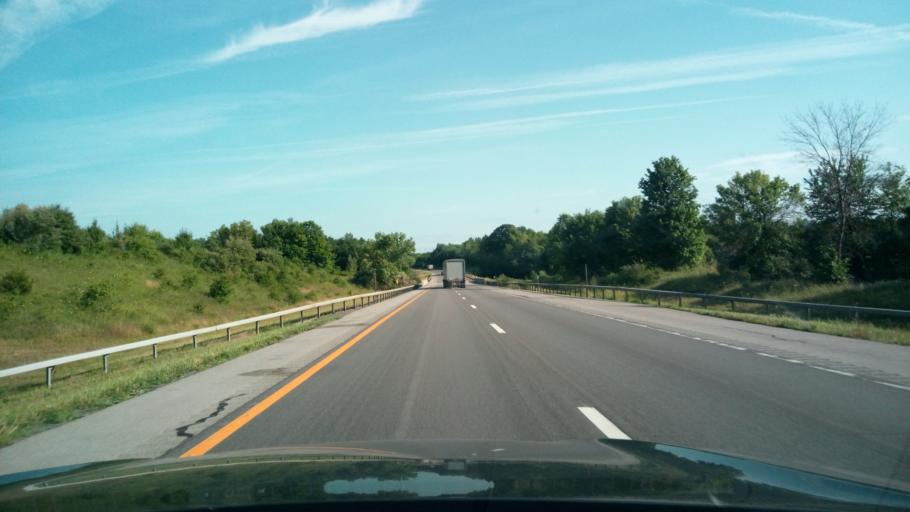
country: US
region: New York
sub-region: Livingston County
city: Dansville
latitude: 42.5937
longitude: -77.7490
